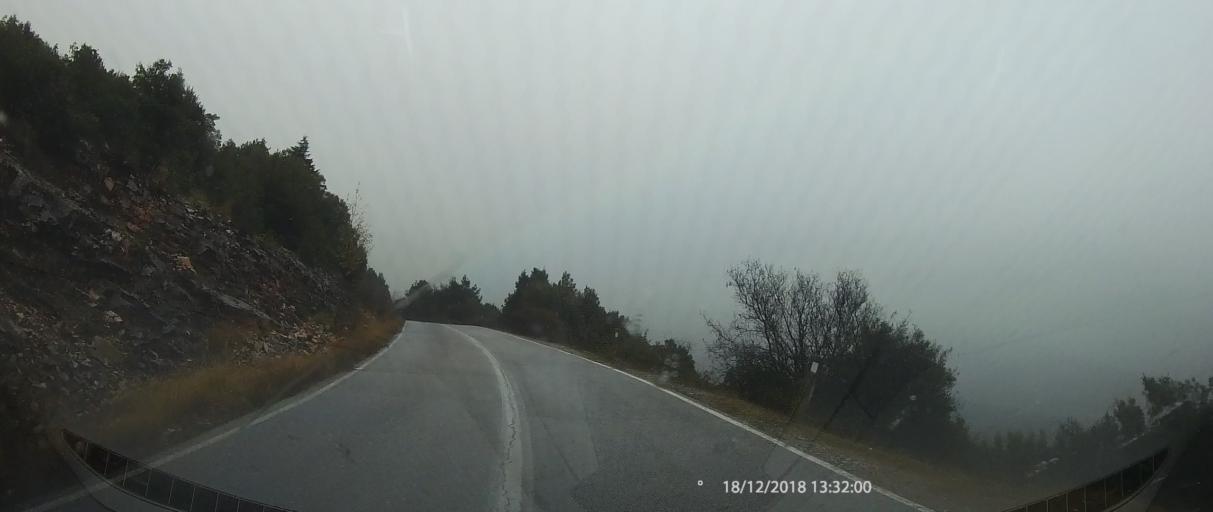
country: GR
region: Central Macedonia
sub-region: Nomos Pierias
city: Litochoro
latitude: 40.1129
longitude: 22.4804
